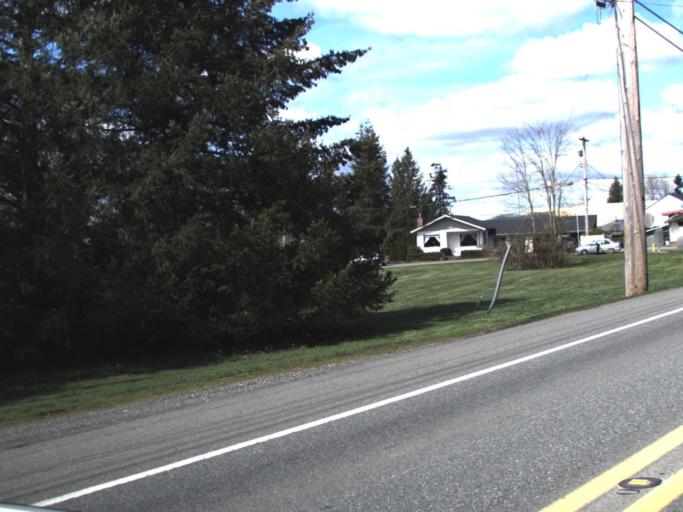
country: US
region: Washington
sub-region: King County
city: Black Diamond
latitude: 47.3080
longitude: -122.0032
